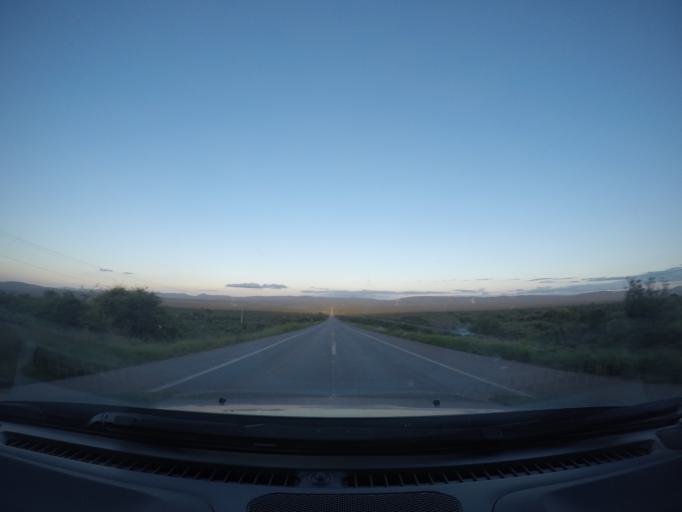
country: BR
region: Bahia
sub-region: Seabra
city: Seabra
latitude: -12.4117
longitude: -41.9728
